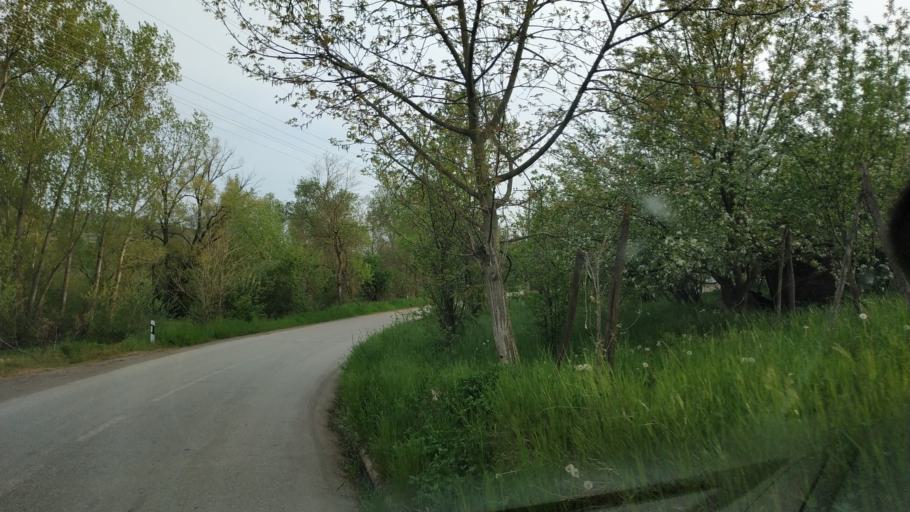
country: RS
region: Central Serbia
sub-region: Nisavski Okrug
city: Aleksinac
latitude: 43.4948
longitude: 21.8215
